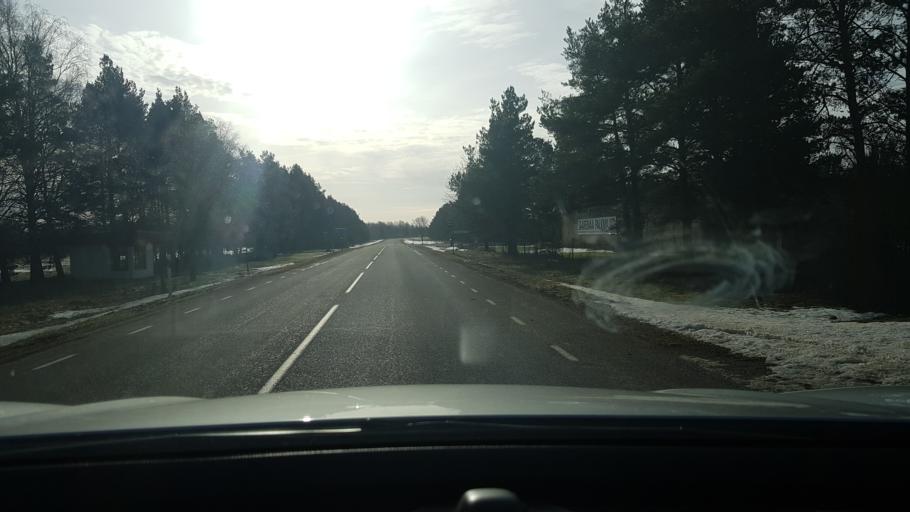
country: EE
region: Saare
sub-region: Kuressaare linn
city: Kuressaare
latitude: 58.5148
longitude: 22.7045
